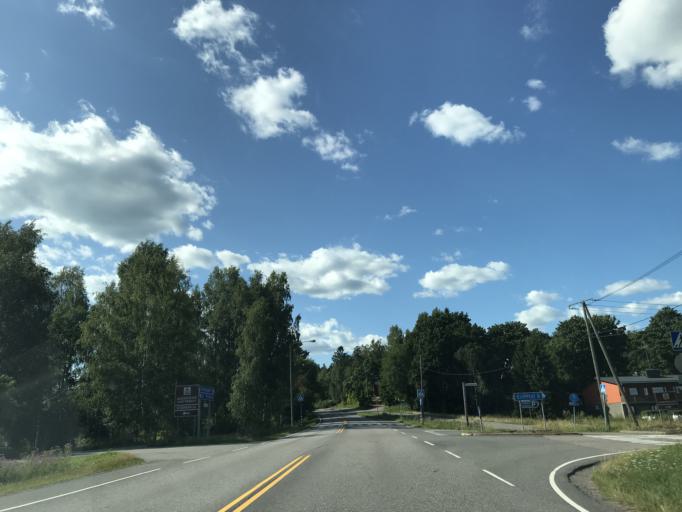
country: FI
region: Uusimaa
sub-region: Helsinki
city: Nurmijaervi
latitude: 60.4213
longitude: 24.8679
